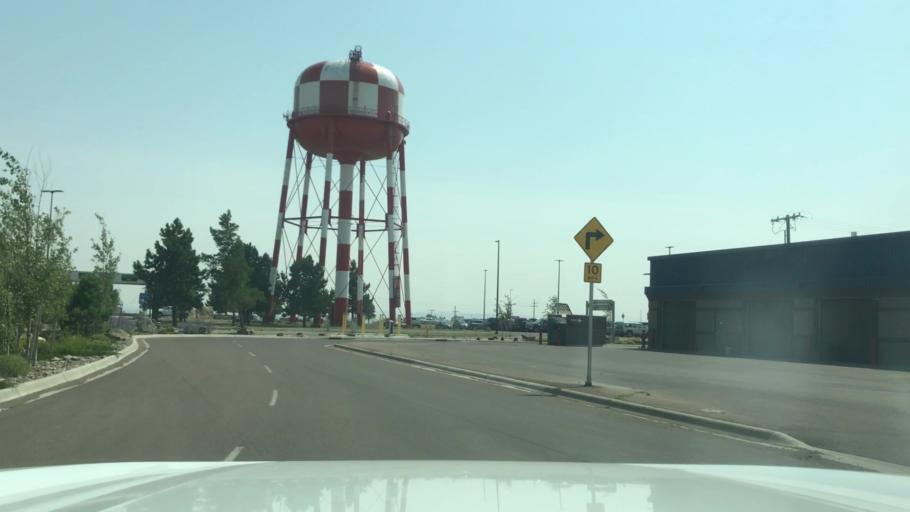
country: US
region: Montana
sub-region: Cascade County
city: Great Falls
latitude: 47.4803
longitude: -111.3584
